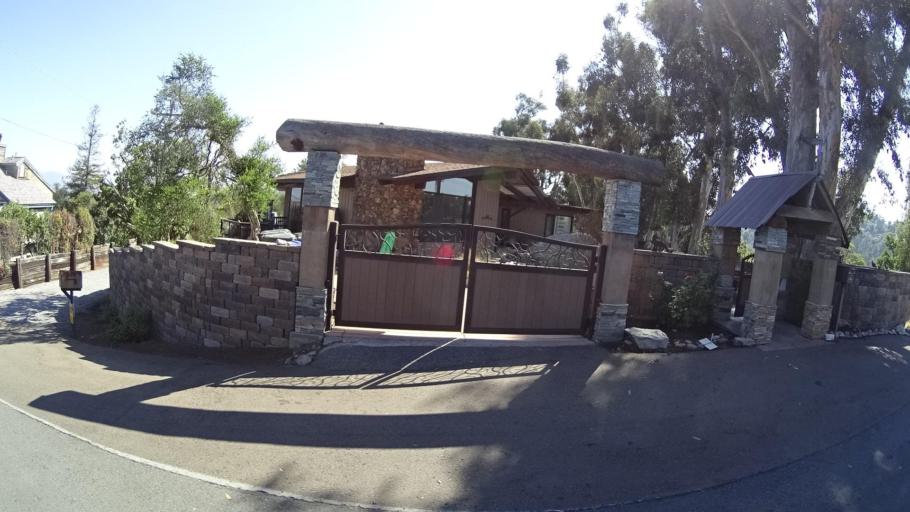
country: US
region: California
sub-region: San Diego County
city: Casa de Oro-Mount Helix
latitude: 32.7743
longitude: -116.9879
